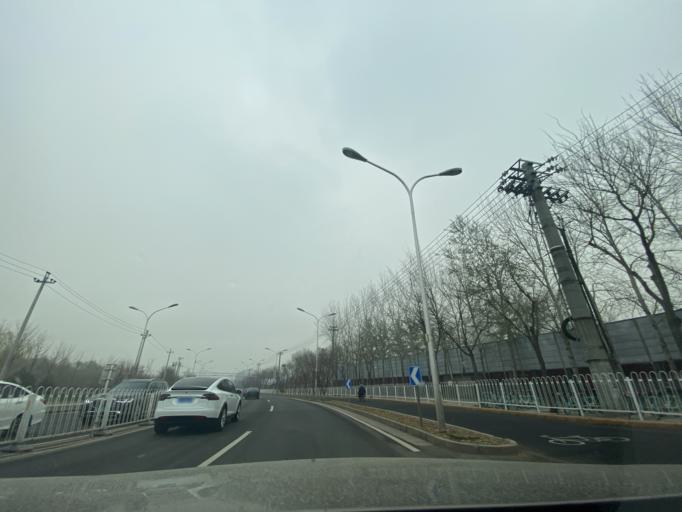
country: CN
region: Beijing
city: Sijiqing
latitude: 39.9686
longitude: 116.2599
